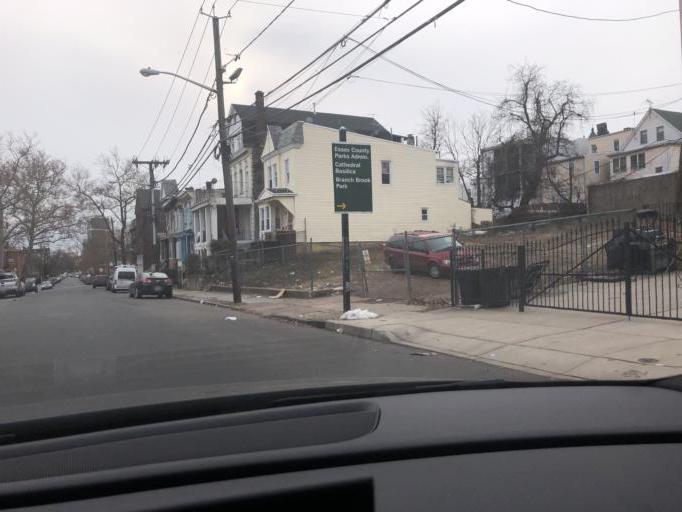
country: US
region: New Jersey
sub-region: Hudson County
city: East Newark
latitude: 40.7569
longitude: -74.1758
